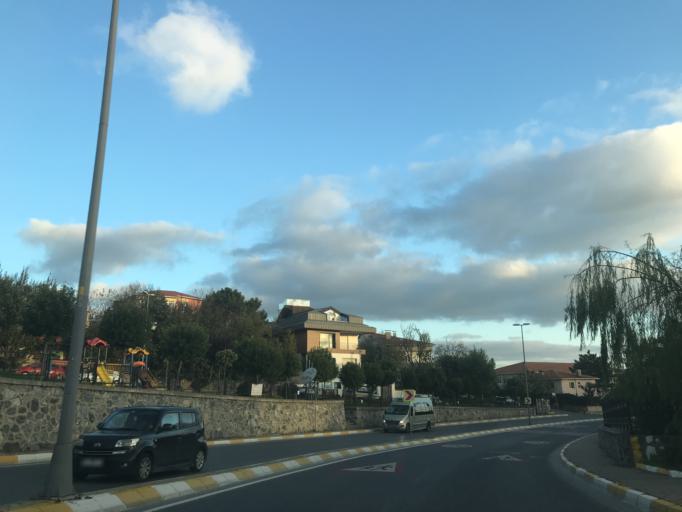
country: TR
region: Istanbul
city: Sisli
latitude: 41.1359
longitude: 29.0396
